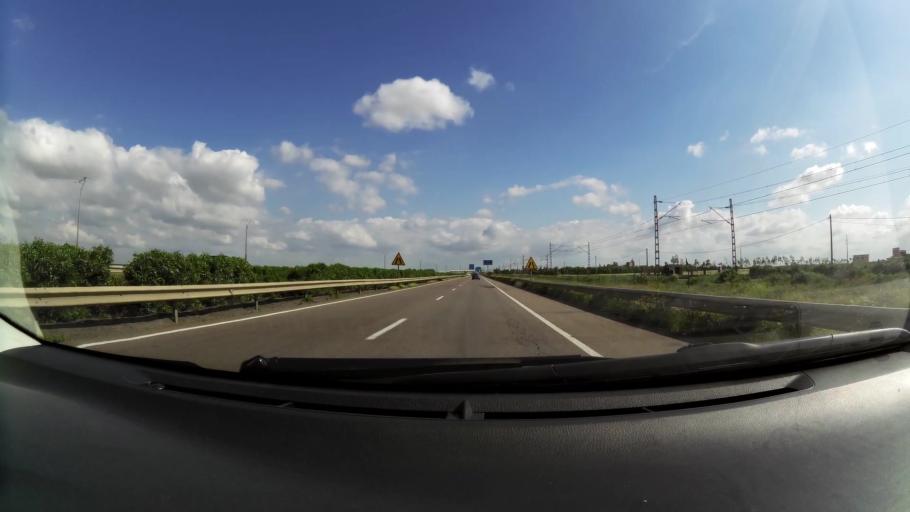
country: MA
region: Chaouia-Ouardigha
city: Nouaseur
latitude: 33.3318
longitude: -7.6090
